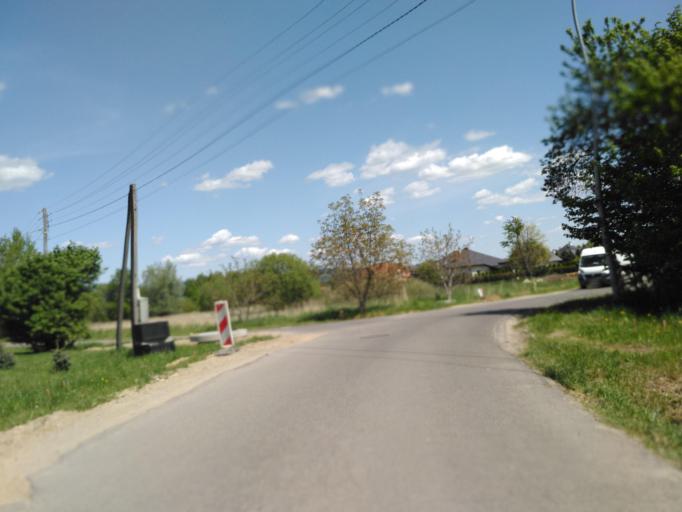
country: PL
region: Subcarpathian Voivodeship
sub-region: Powiat krosnienski
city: Odrzykon
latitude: 49.7209
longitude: 21.7175
